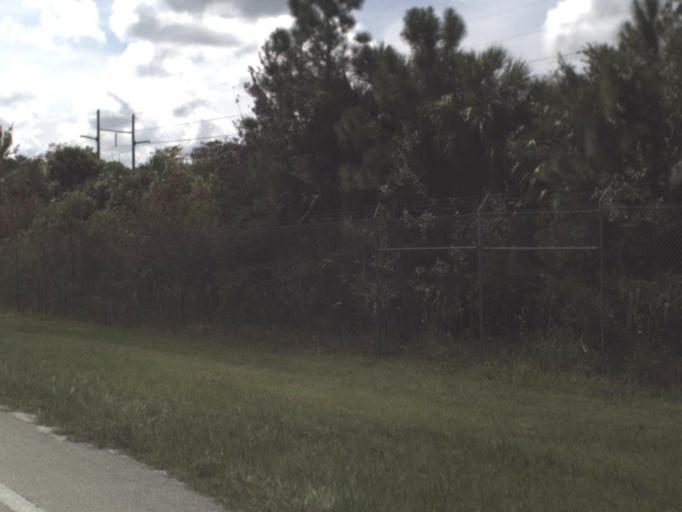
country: US
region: Florida
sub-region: Collier County
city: Immokalee
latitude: 26.1922
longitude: -81.3460
